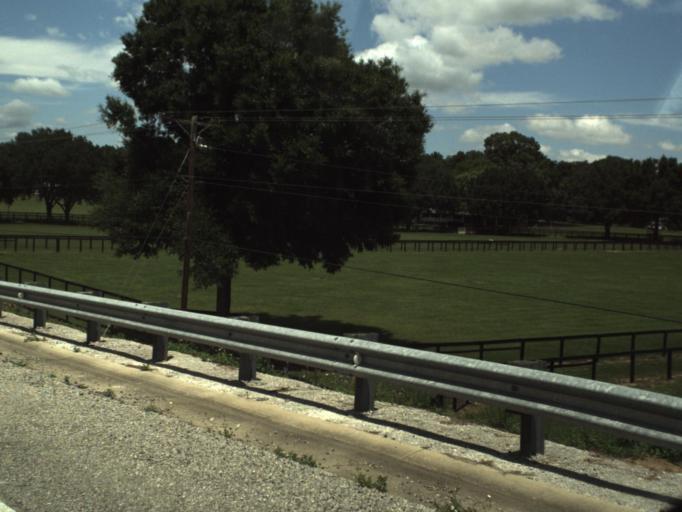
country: US
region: Florida
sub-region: Marion County
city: Citra
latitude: 29.3998
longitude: -82.2037
